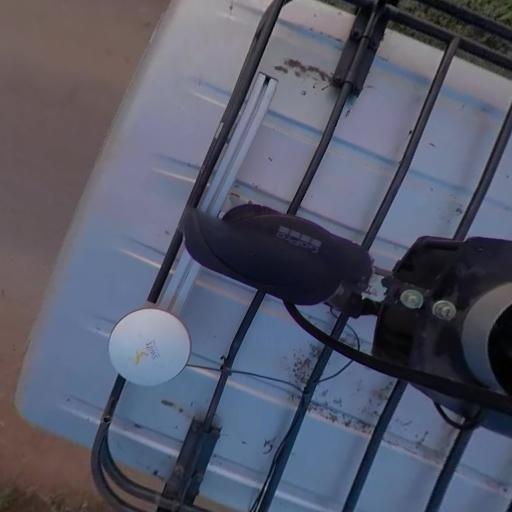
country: IN
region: Telangana
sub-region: Nalgonda
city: Suriapet
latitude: 17.0580
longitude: 79.5481
